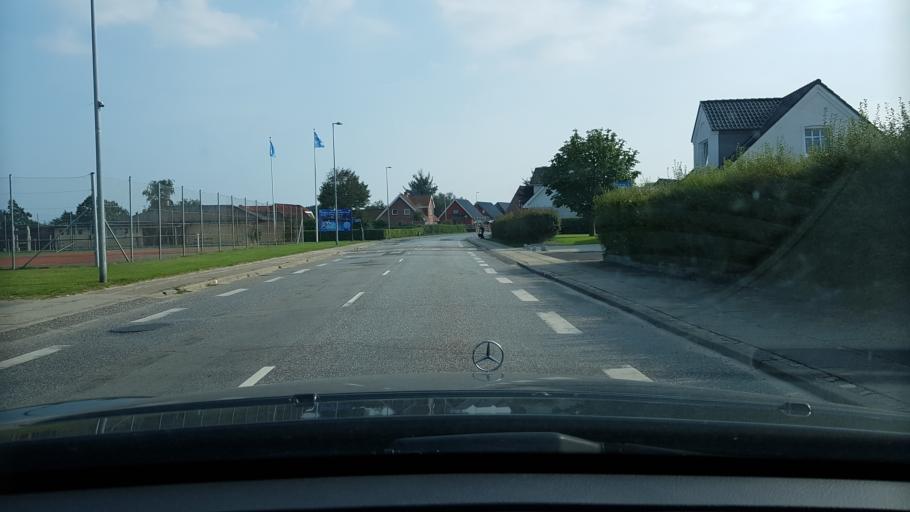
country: DK
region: North Denmark
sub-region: Mariagerfjord Kommune
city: Hadsund
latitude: 56.8070
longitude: 10.2708
